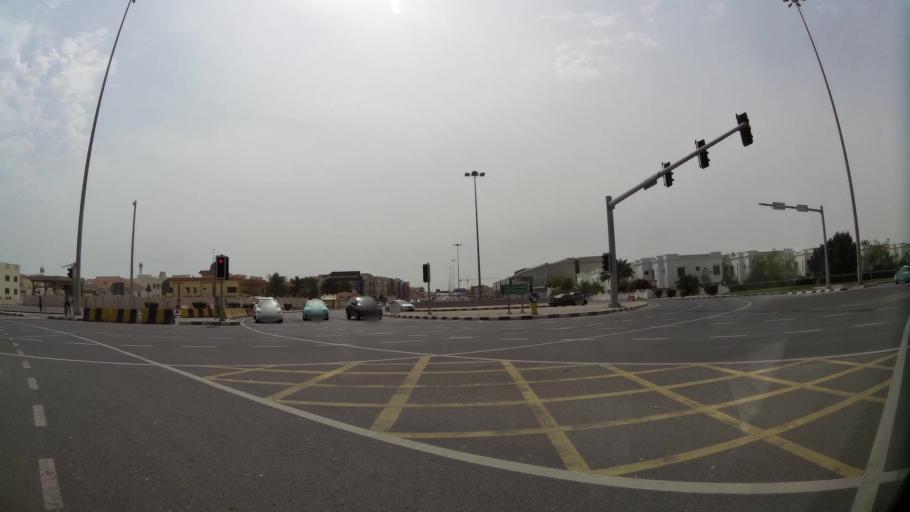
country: QA
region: Baladiyat ad Dawhah
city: Doha
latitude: 25.2757
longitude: 51.4890
